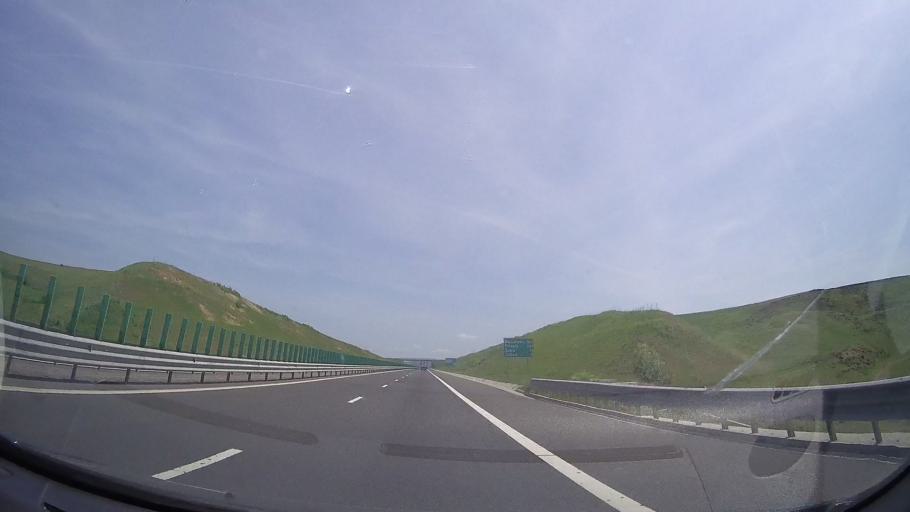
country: RO
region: Alba
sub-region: Comuna Pianu
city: Pianu de Jos
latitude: 45.9694
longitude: 23.4901
